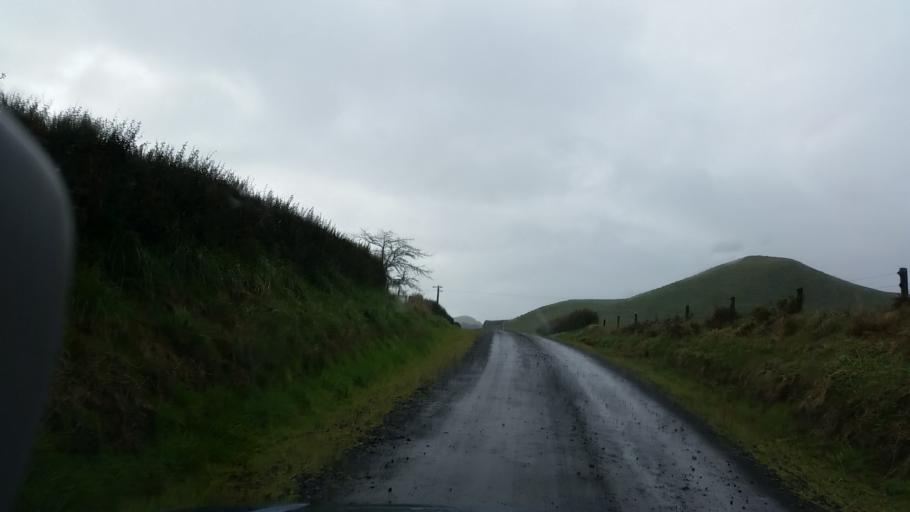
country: NZ
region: Taranaki
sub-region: South Taranaki District
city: Eltham
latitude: -39.3471
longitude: 174.4383
